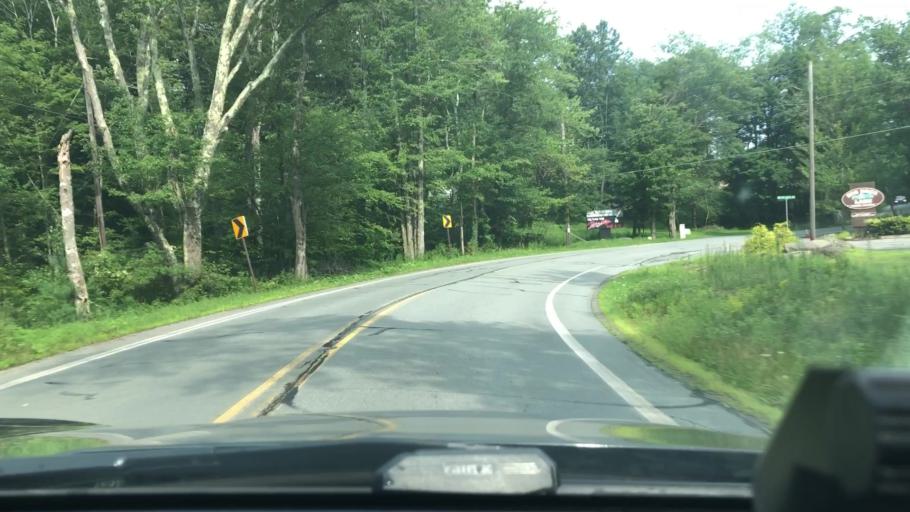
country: US
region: Pennsylvania
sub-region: Lackawanna County
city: Moscow
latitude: 41.2493
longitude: -75.4929
